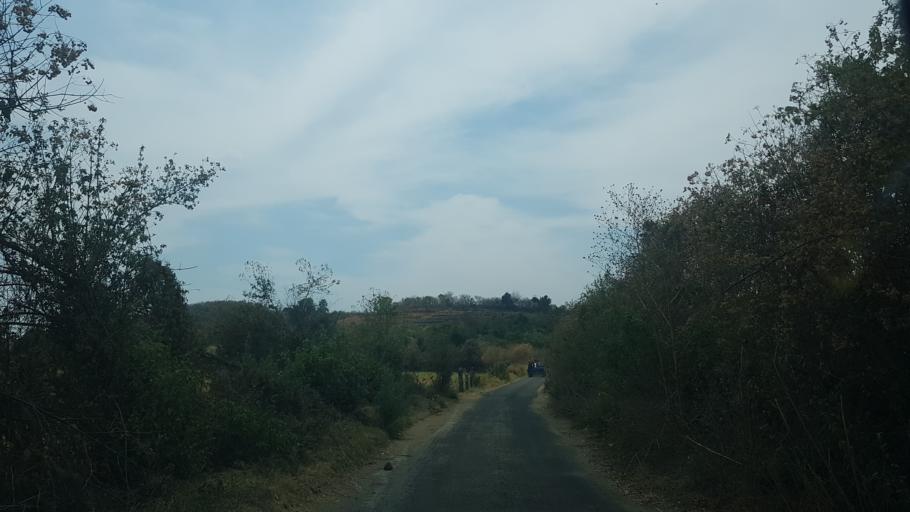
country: MX
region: Puebla
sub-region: Atzitzihuacan
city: Santiago Atzitzihuacan
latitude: 18.8526
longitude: -98.6118
